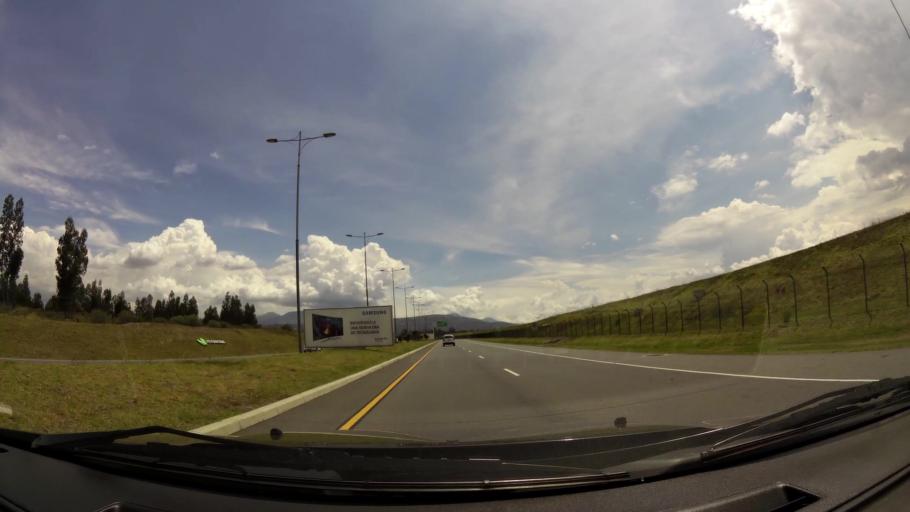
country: EC
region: Pichincha
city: Quito
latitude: -0.1516
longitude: -78.3512
